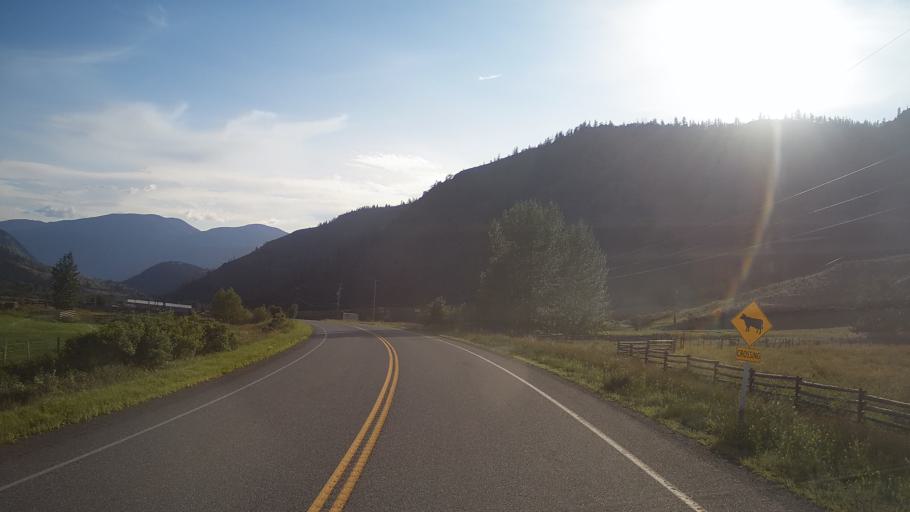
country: CA
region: British Columbia
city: Lillooet
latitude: 50.8987
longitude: -121.7870
